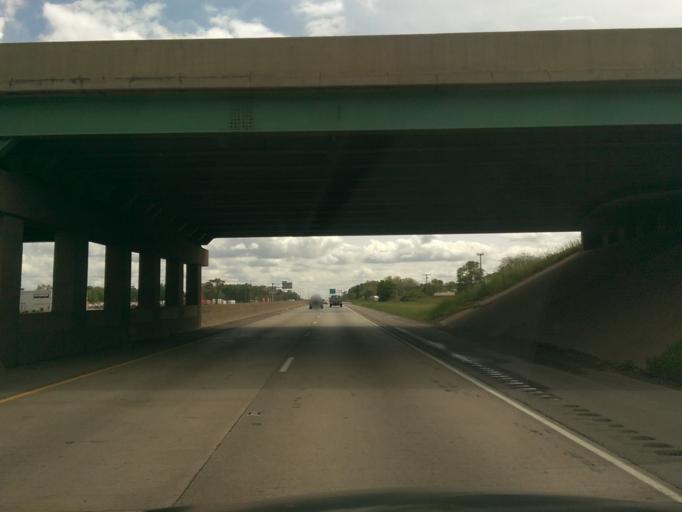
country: US
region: Indiana
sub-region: Lake County
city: Highland
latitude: 41.5885
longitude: -87.4330
